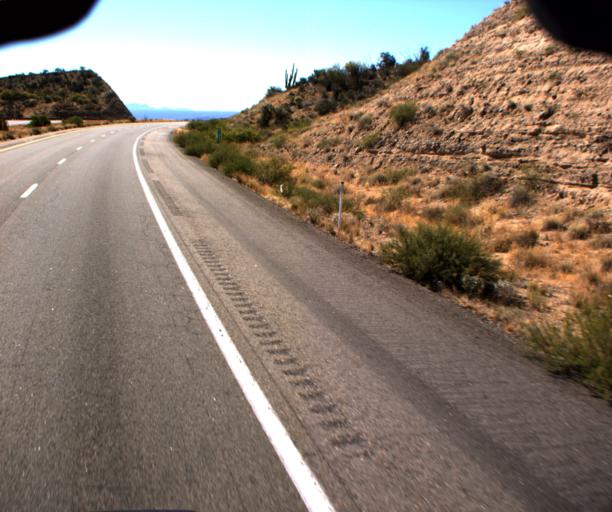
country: US
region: Arizona
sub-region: Yavapai County
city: Bagdad
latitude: 34.4447
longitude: -113.2715
